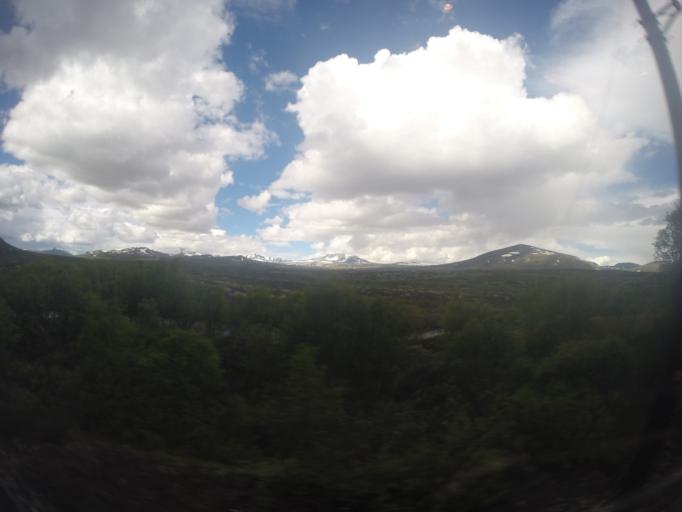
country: NO
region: Oppland
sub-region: Dovre
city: Dovre
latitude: 62.2373
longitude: 9.5291
